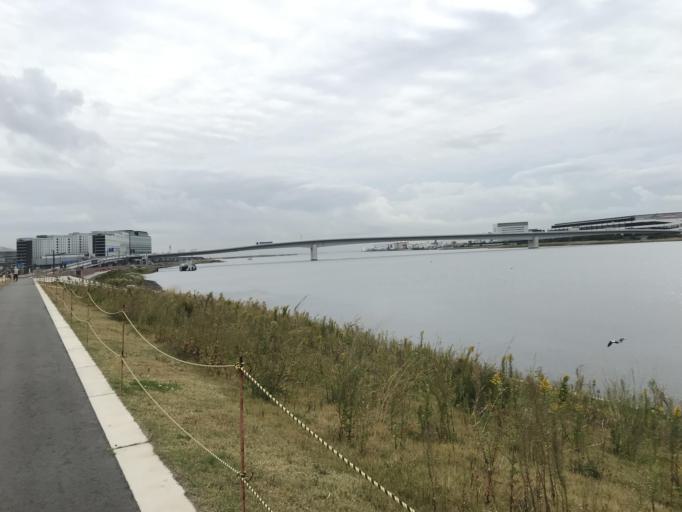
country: JP
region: Kanagawa
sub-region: Kawasaki-shi
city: Kawasaki
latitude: 35.5454
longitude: 139.7573
